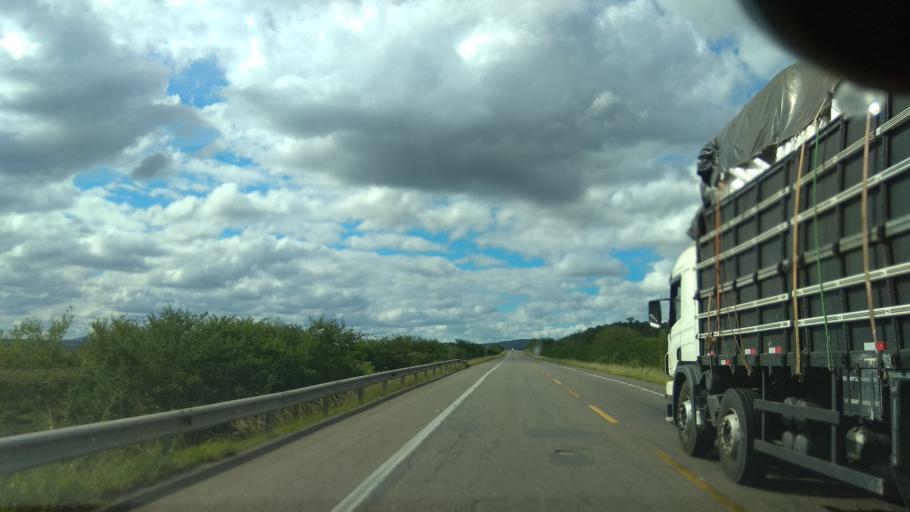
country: BR
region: Bahia
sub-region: Amargosa
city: Amargosa
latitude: -12.9440
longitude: -39.9123
